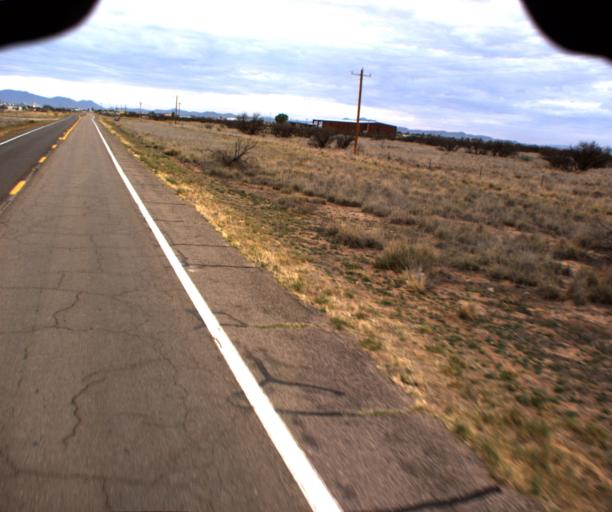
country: US
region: Arizona
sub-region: Cochise County
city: Willcox
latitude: 32.2742
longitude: -109.8176
